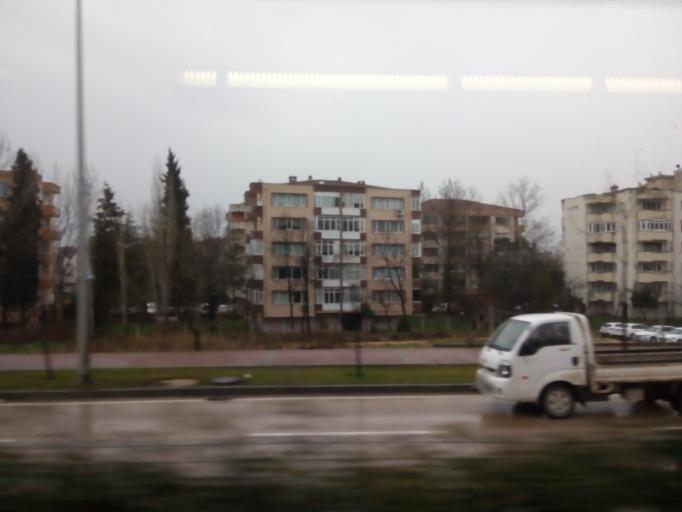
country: TR
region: Bursa
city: Yildirim
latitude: 40.2067
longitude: 29.0285
